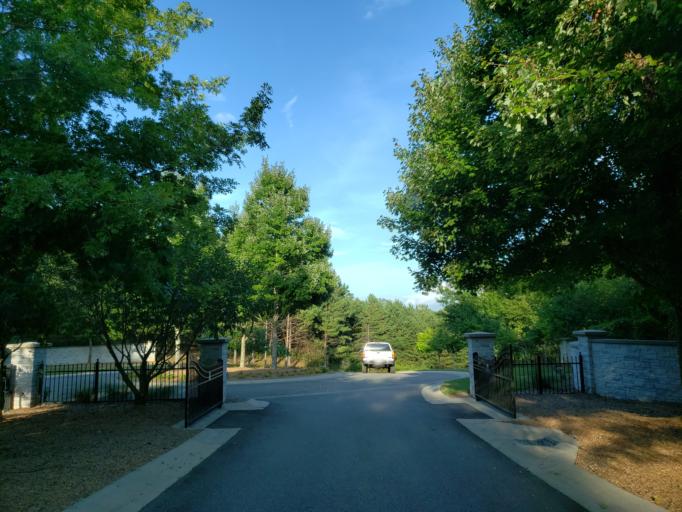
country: US
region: Georgia
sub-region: Cherokee County
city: Canton
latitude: 34.2334
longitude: -84.5745
